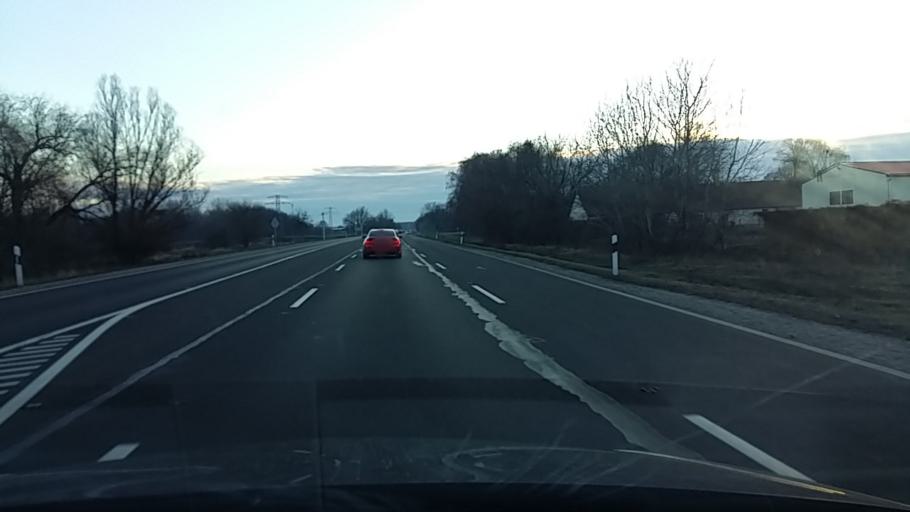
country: HU
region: Hajdu-Bihar
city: Hajduhadhaz
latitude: 47.6907
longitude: 21.6549
